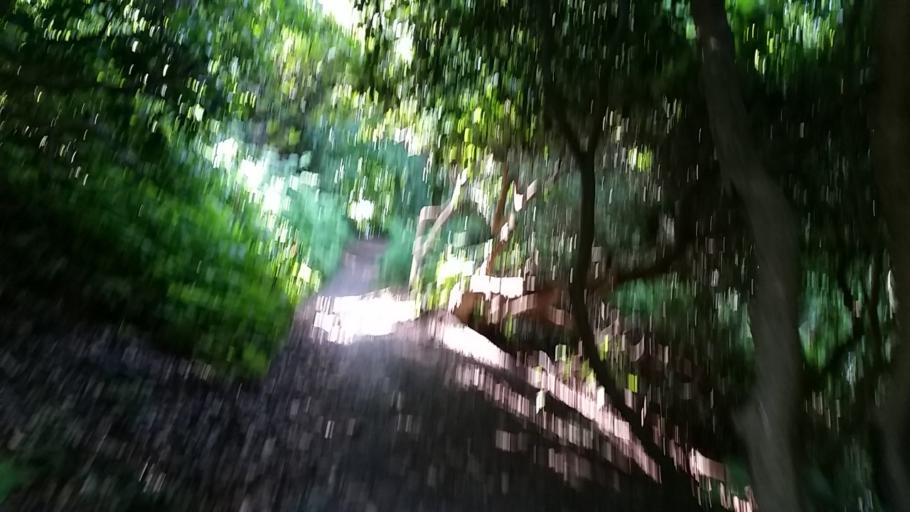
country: DE
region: Schleswig-Holstein
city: Halstenbek
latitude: 53.5610
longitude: 9.7936
